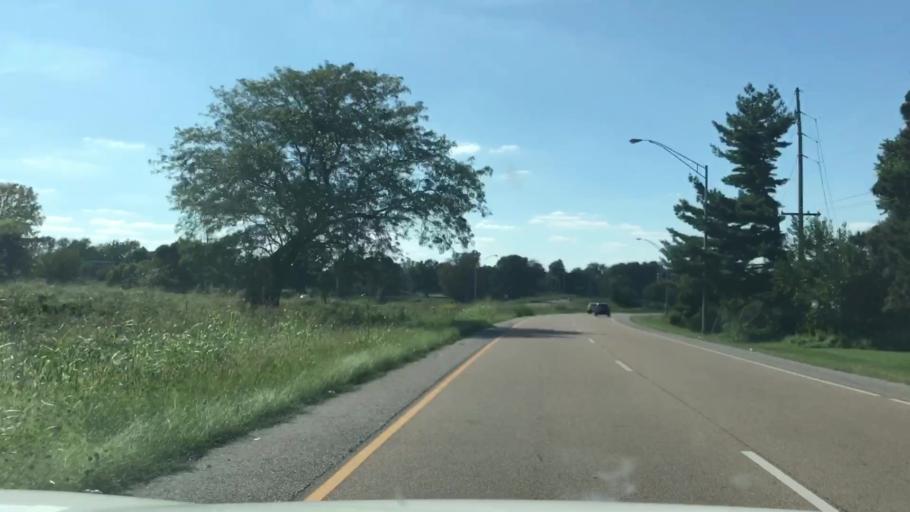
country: US
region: Illinois
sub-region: Saint Clair County
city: Alorton
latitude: 38.5478
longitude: -90.0622
